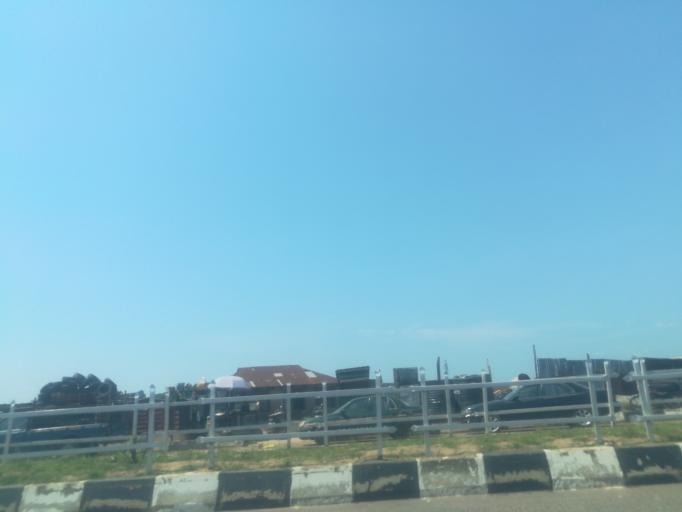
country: NG
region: Ogun
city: Abeokuta
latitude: 7.1632
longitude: 3.3508
